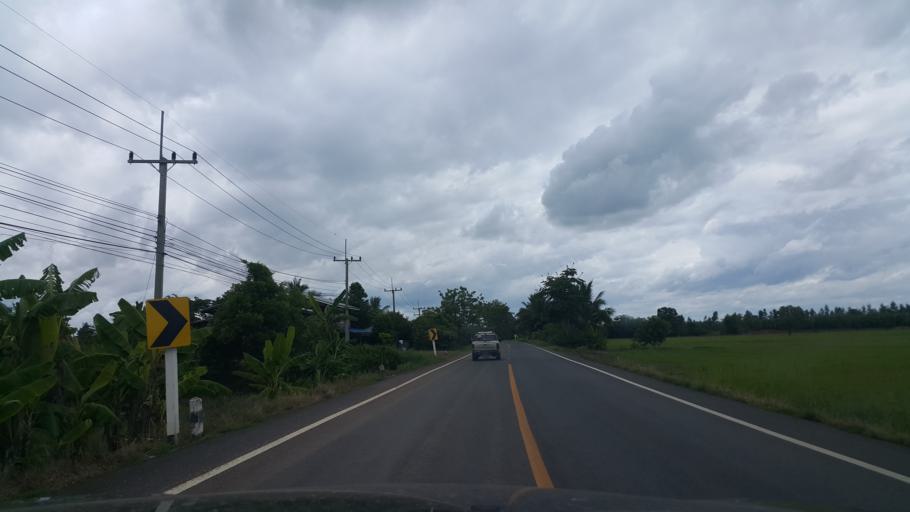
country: TH
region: Sukhothai
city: Sukhothai
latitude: 16.9168
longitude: 99.8574
